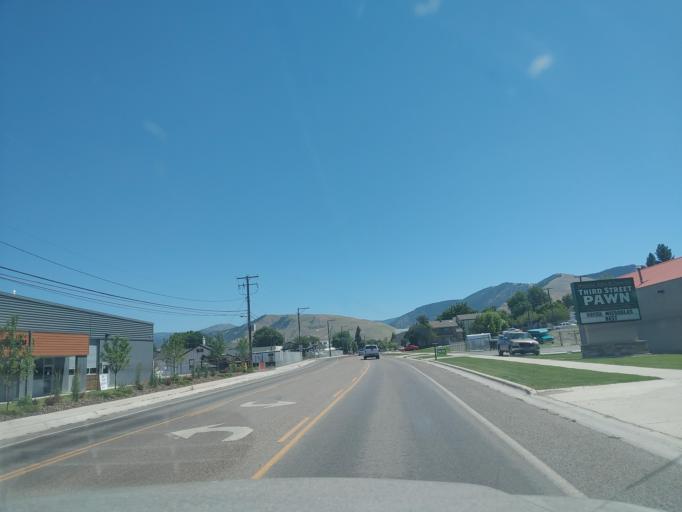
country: US
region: Montana
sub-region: Missoula County
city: Orchard Homes
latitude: 46.8669
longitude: -114.0299
